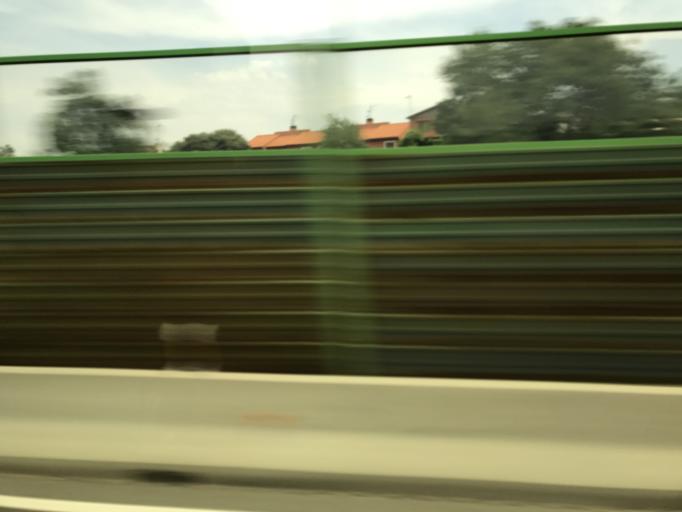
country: ES
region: Madrid
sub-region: Provincia de Madrid
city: La Cabrera
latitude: 40.9238
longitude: -3.6178
